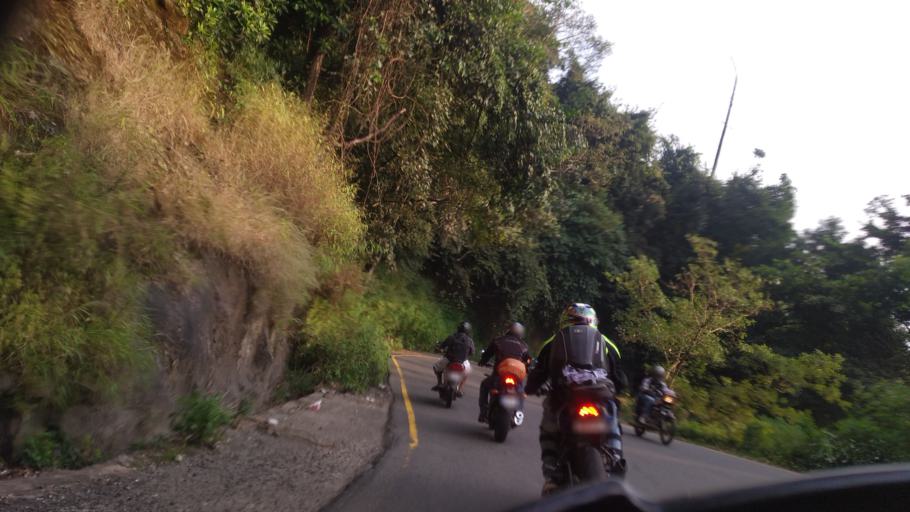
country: IN
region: Kerala
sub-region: Wayanad
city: Kalpetta
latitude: 11.5149
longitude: 76.0151
